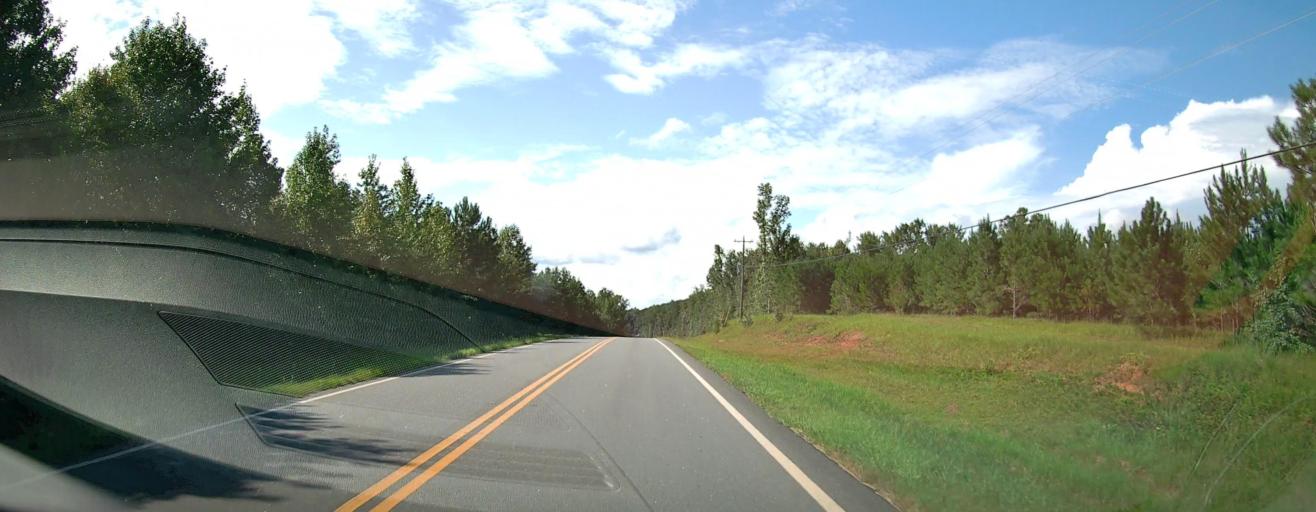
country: US
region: Georgia
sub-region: Upson County
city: Hannahs Mill
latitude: 32.9258
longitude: -84.4414
